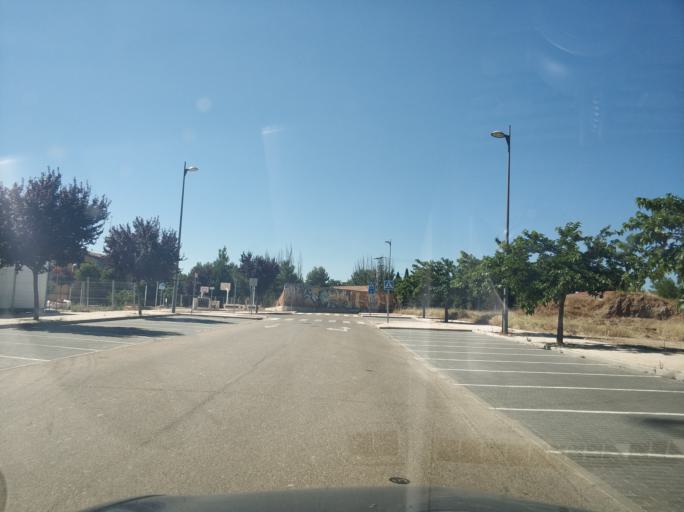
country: ES
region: Castille and Leon
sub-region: Provincia de Salamanca
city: Salamanca
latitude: 40.9814
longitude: -5.6571
